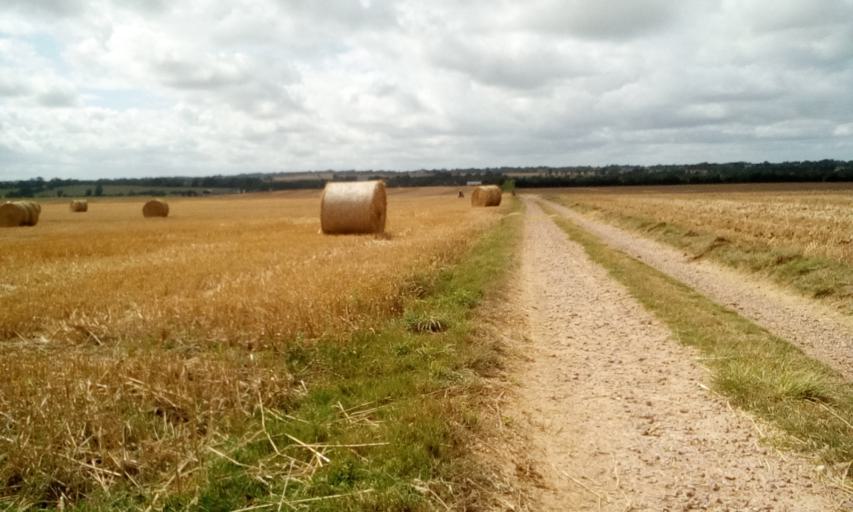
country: FR
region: Lower Normandy
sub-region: Departement du Calvados
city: Tilly-sur-Seulles
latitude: 49.2035
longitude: -0.6147
